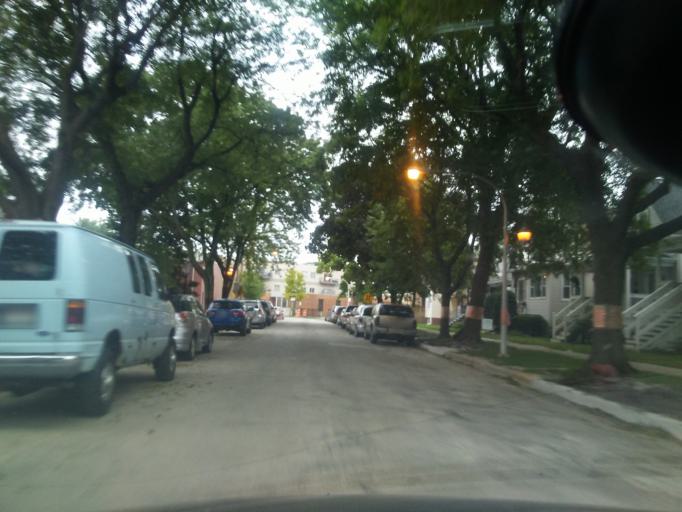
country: US
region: Illinois
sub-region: Cook County
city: Lincolnwood
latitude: 41.9690
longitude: -87.7451
